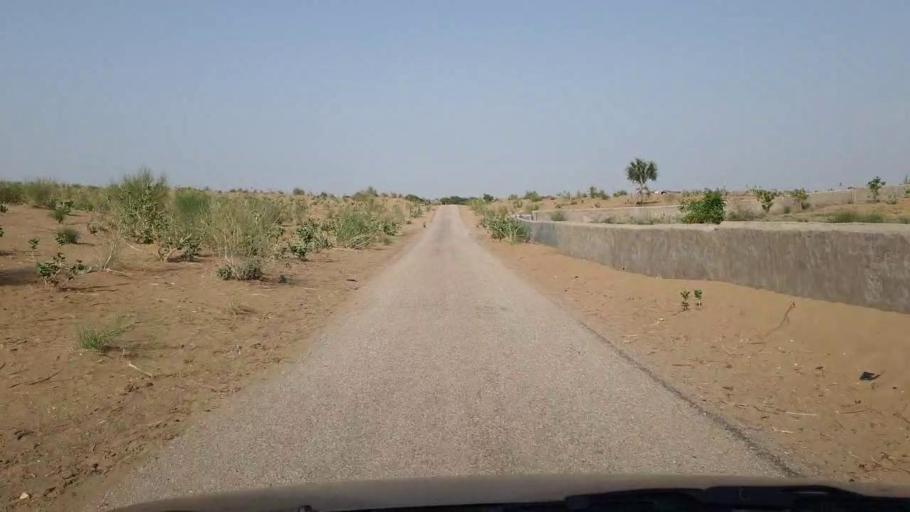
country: PK
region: Sindh
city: Chor
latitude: 25.4529
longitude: 70.5282
